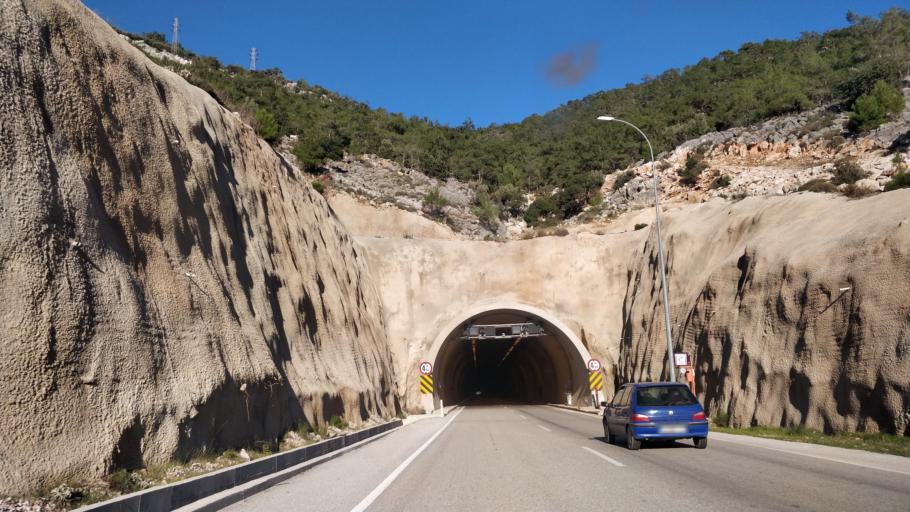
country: TR
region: Mersin
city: Akdere
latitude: 36.2579
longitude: 33.7922
